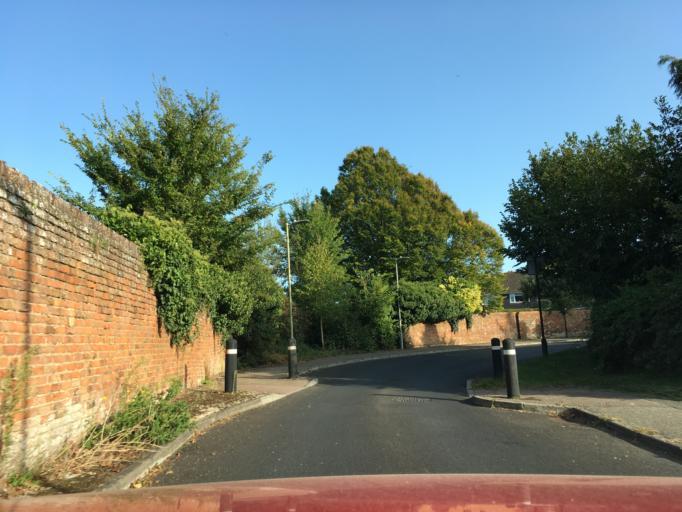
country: GB
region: England
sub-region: Gloucestershire
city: Gloucester
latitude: 51.8503
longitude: -2.2680
